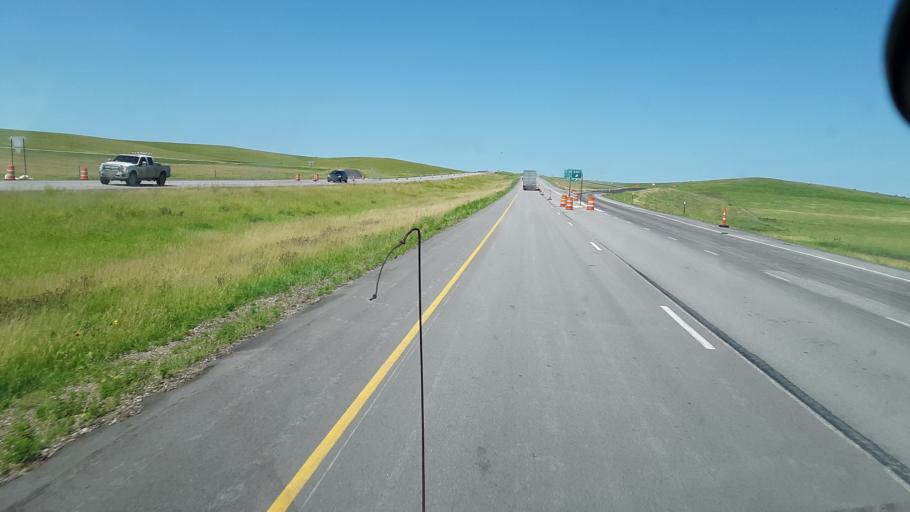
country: US
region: South Dakota
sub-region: Lyman County
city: Kennebec
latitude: 43.9130
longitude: -100.2794
